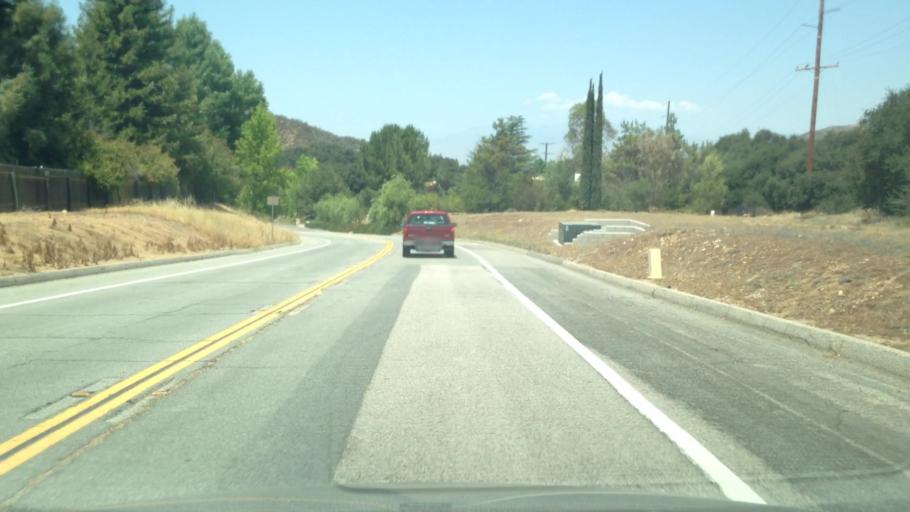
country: US
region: California
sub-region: Riverside County
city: Cherry Valley
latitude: 34.0104
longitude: -116.9898
